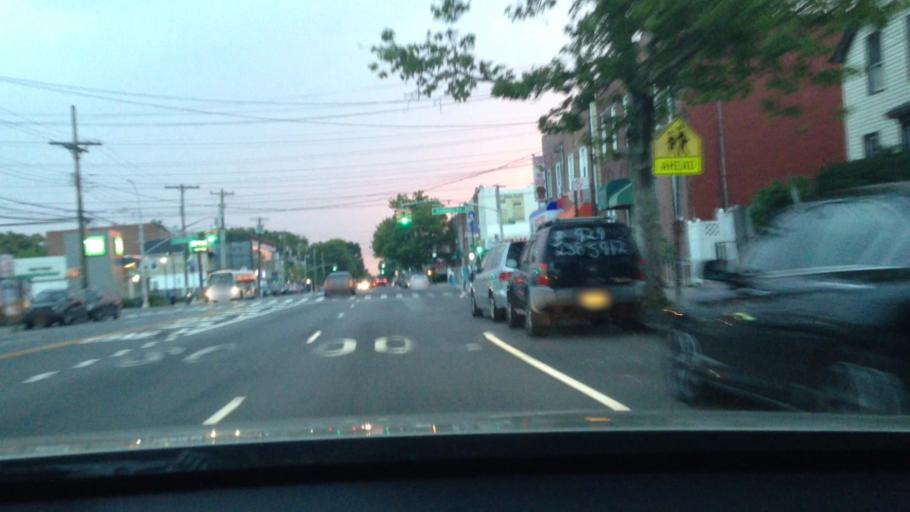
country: US
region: New York
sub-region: Kings County
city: East New York
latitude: 40.6398
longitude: -73.9066
